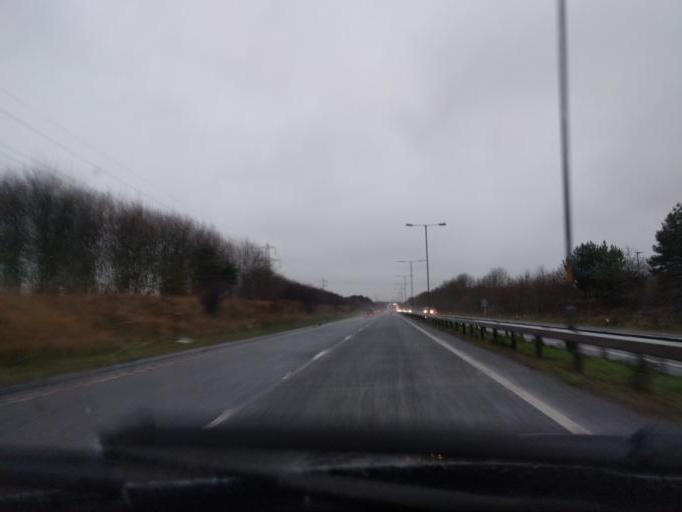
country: GB
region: England
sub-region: Northumberland
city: Newbiggin-by-the-Sea
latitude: 55.1663
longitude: -1.5355
